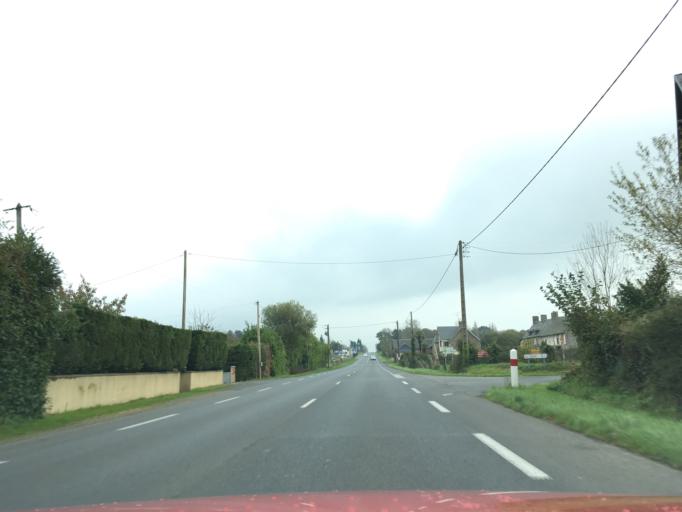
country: FR
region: Lower Normandy
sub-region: Departement de la Manche
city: Saint-Jean-des-Champs
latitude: 48.8370
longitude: -1.4903
